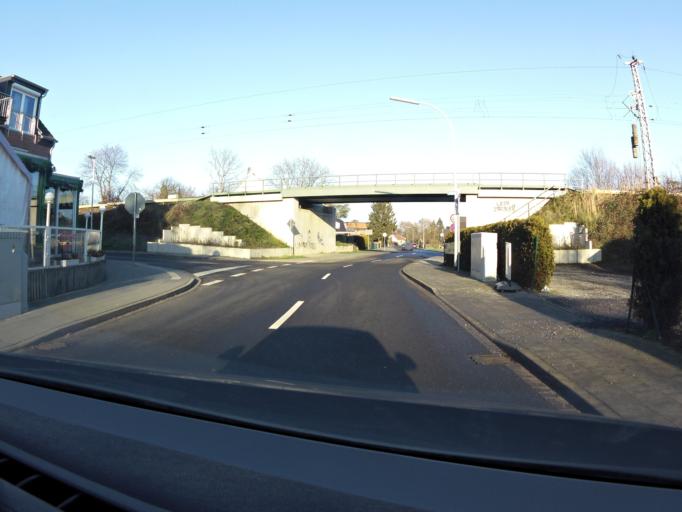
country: DE
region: North Rhine-Westphalia
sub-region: Regierungsbezirk Dusseldorf
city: Nettetal
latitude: 51.2923
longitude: 6.2442
